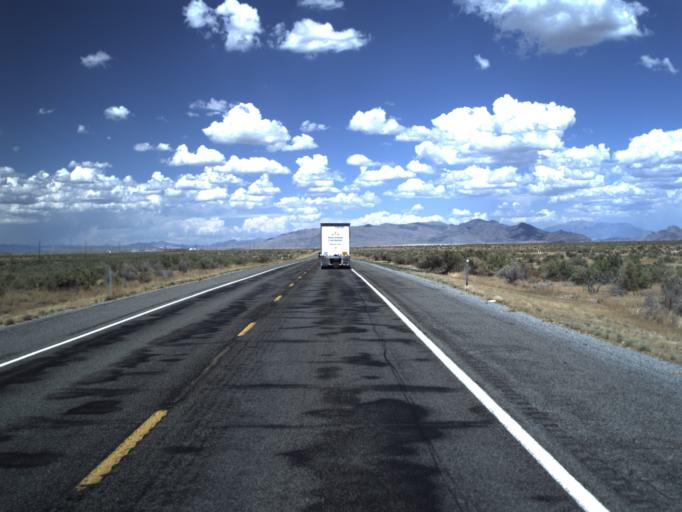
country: US
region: Utah
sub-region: Millard County
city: Delta
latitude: 39.4379
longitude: -112.4586
